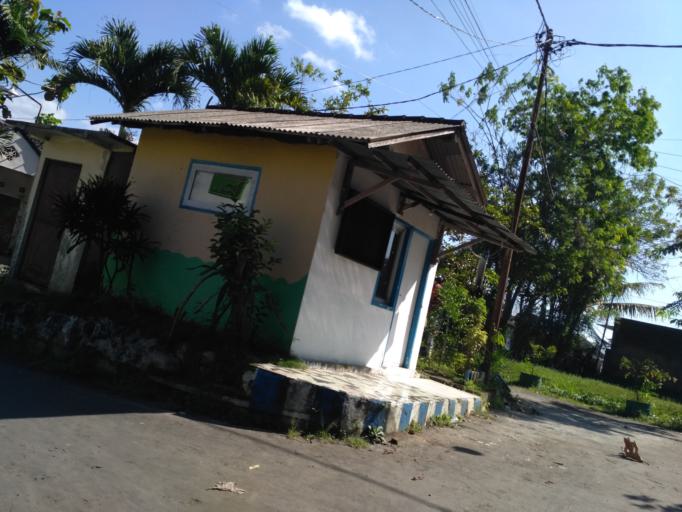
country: ID
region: East Java
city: Singosari
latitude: -7.9144
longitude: 112.6714
